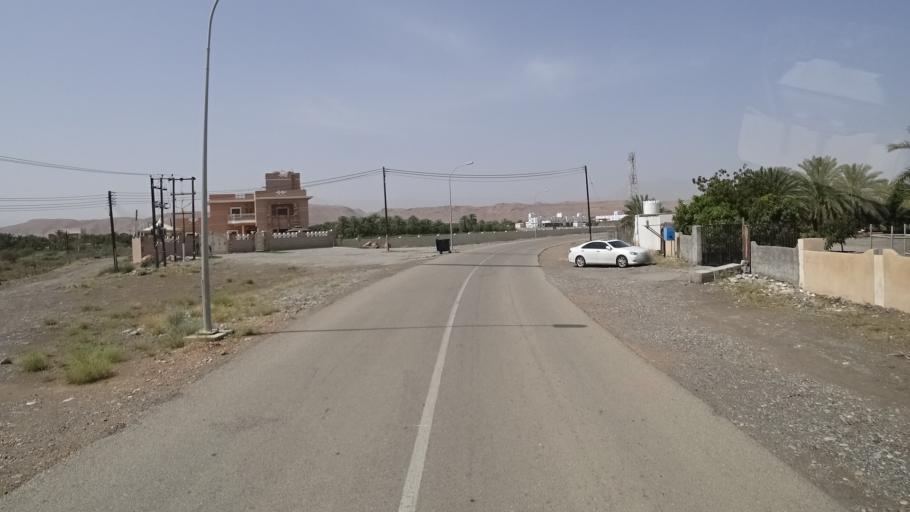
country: OM
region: Muhafazat Masqat
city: Muscat
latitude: 23.2078
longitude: 58.9704
